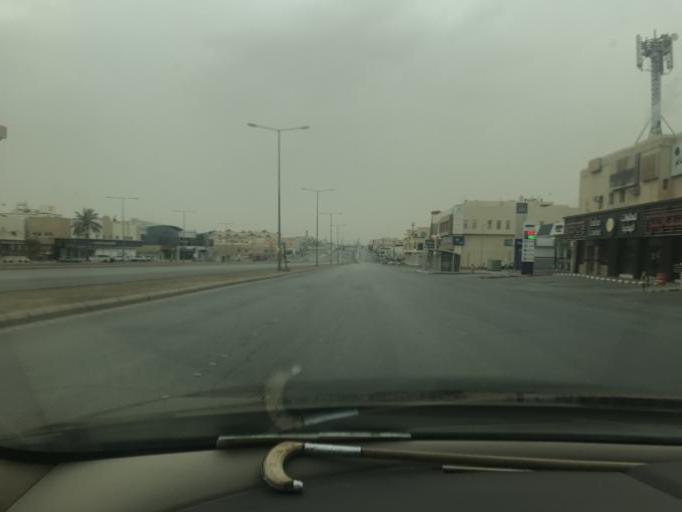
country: SA
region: Ar Riyad
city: Riyadh
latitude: 24.7703
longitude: 46.7120
